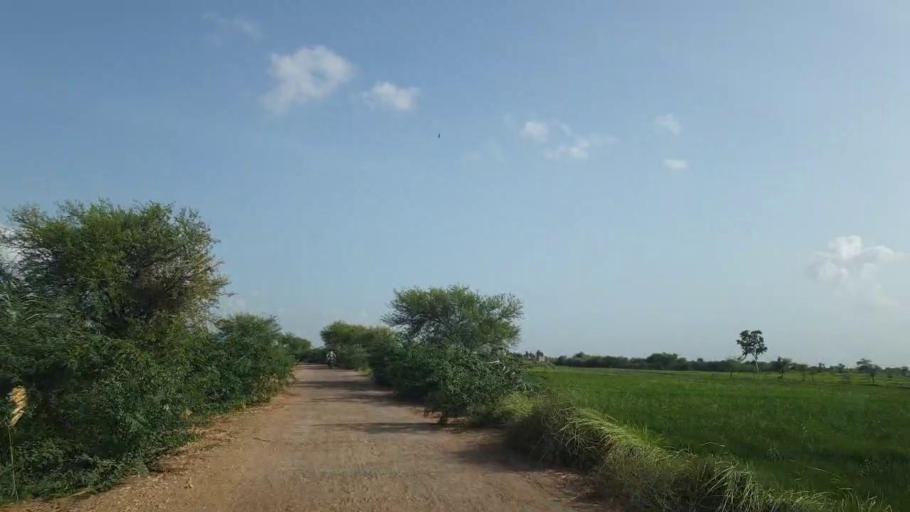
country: PK
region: Sindh
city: Kadhan
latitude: 24.6189
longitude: 69.0958
